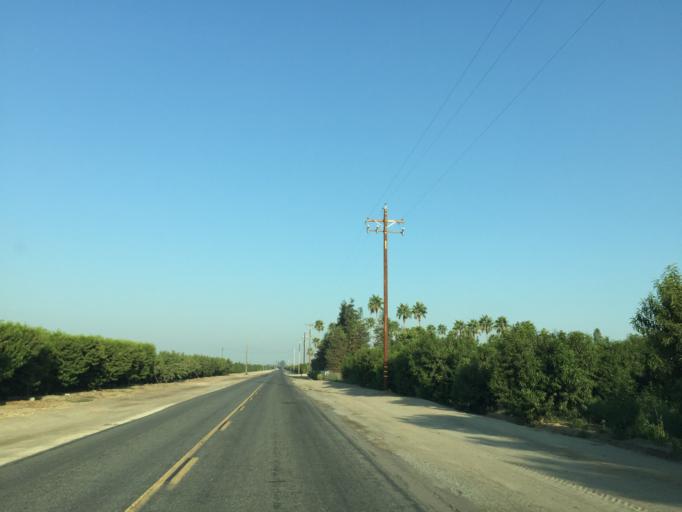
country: US
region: California
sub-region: Tulare County
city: London
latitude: 36.4588
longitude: -119.4571
